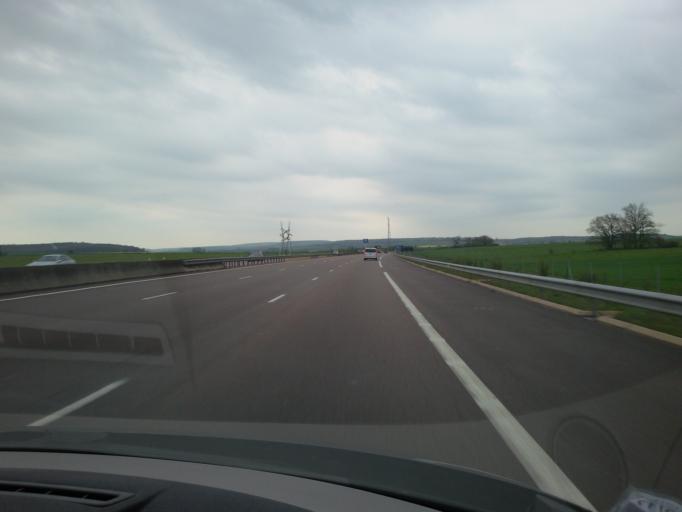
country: FR
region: Champagne-Ardenne
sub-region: Departement de la Haute-Marne
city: Rolampont
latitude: 47.8790
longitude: 5.2204
